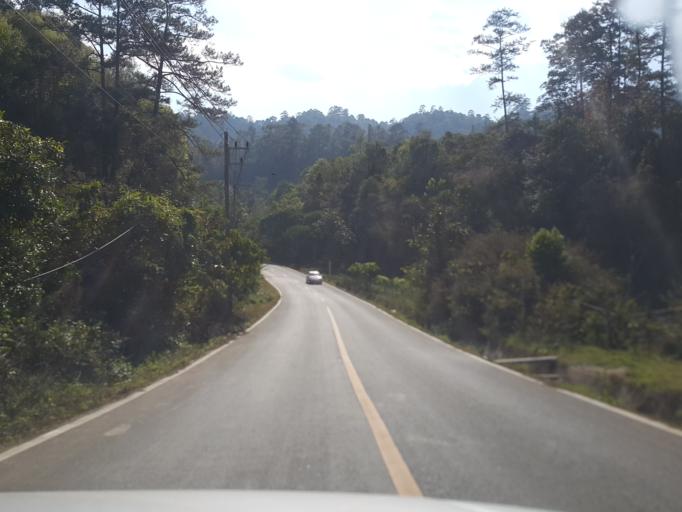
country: TH
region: Chiang Mai
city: Mae Wang
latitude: 18.6873
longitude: 98.5651
